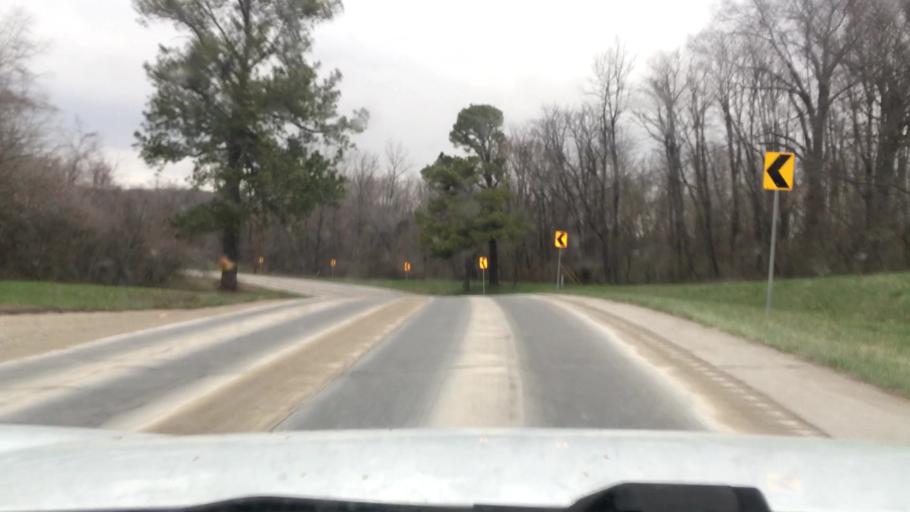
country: US
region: Missouri
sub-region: Saint Charles County
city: Weldon Spring
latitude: 38.6688
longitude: -90.7320
